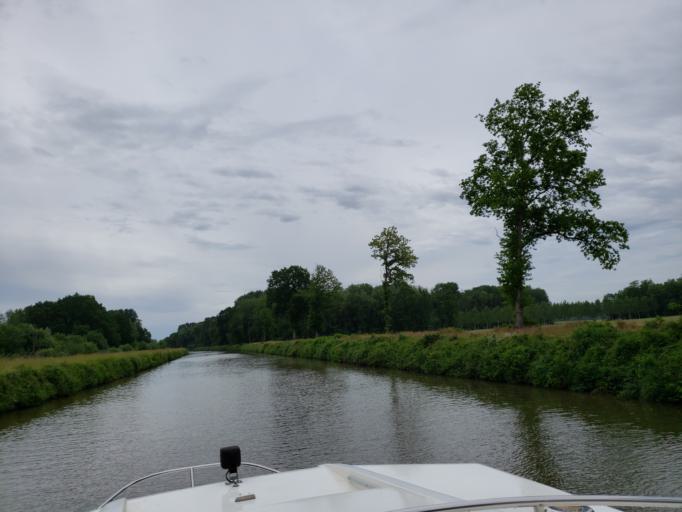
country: FR
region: Bourgogne
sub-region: Departement de l'Yonne
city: Appoigny
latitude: 47.9037
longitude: 3.5345
